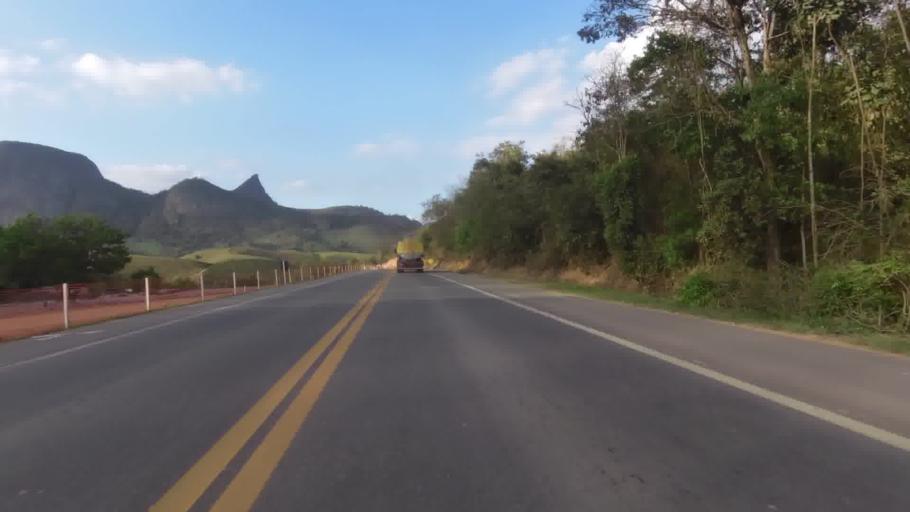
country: BR
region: Espirito Santo
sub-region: Rio Novo Do Sul
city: Rio Novo do Sul
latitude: -20.8980
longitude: -41.0104
